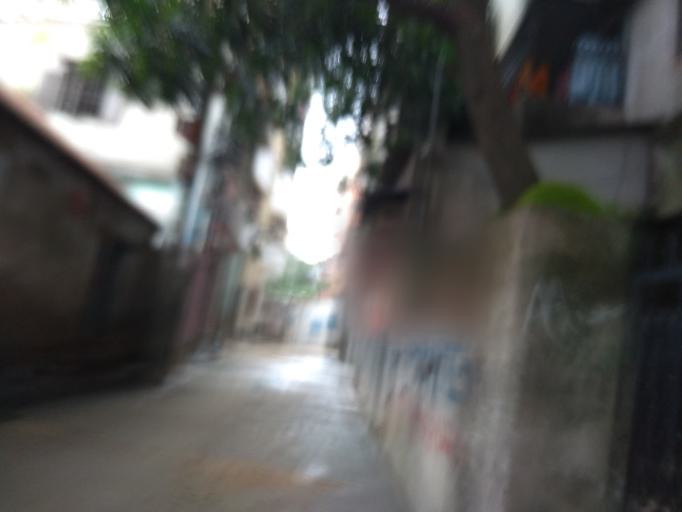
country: BD
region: Dhaka
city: Azimpur
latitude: 23.7927
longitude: 90.3838
